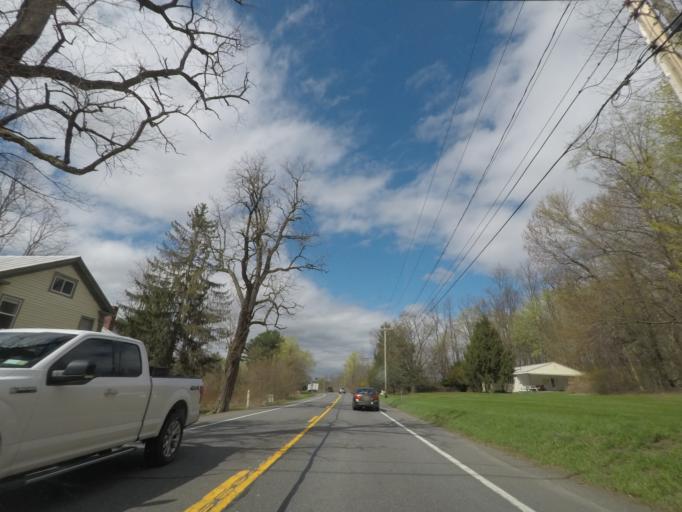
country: US
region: New York
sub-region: Columbia County
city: Niverville
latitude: 42.4664
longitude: -73.6906
